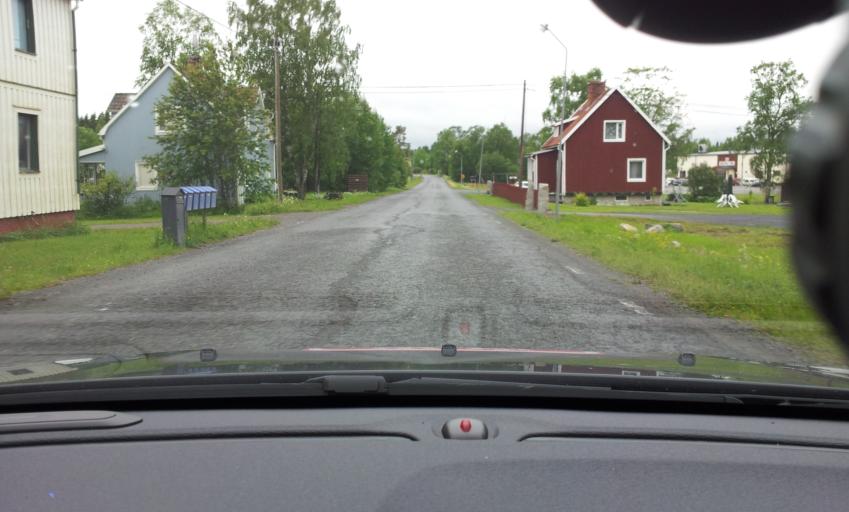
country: SE
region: Jaemtland
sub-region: Stroemsunds Kommun
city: Stroemsund
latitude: 63.6261
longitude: 15.2138
